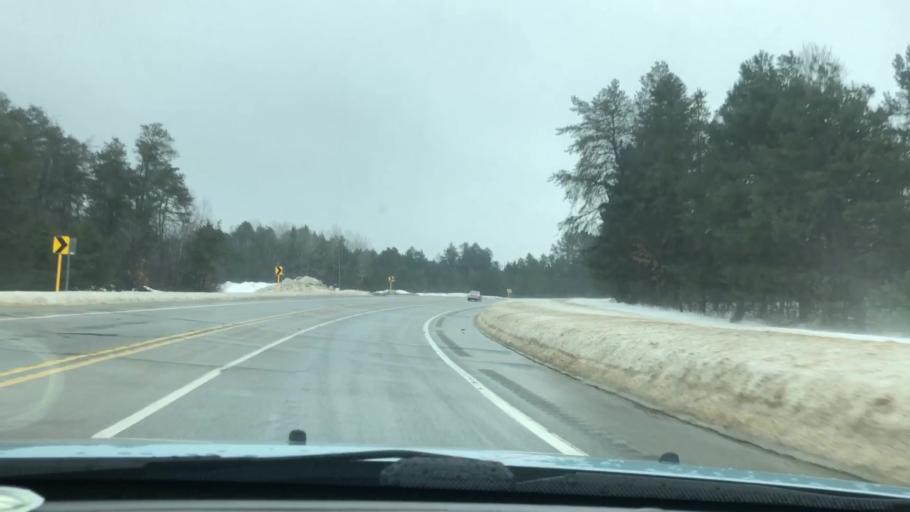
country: US
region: Michigan
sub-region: Otsego County
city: Gaylord
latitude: 45.0607
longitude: -84.7776
